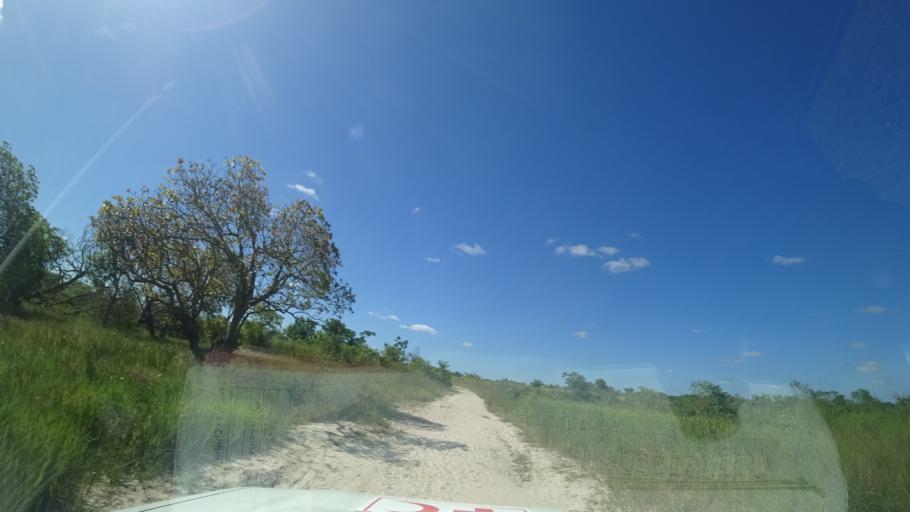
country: MZ
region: Sofala
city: Dondo
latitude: -19.4812
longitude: 34.6252
